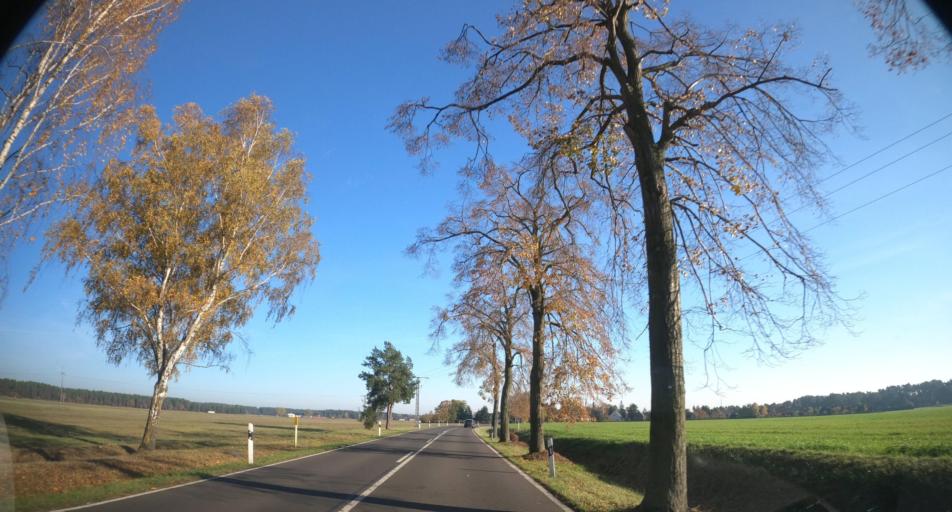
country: DE
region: Mecklenburg-Vorpommern
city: Ahlbeck
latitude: 53.6735
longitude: 14.1754
